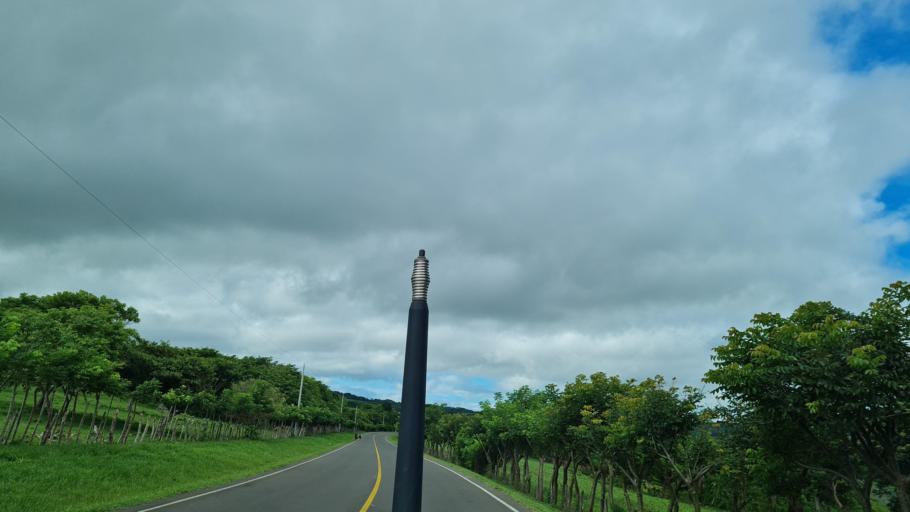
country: NI
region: Boaco
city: San Jose de los Remates
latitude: 12.6028
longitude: -85.8987
